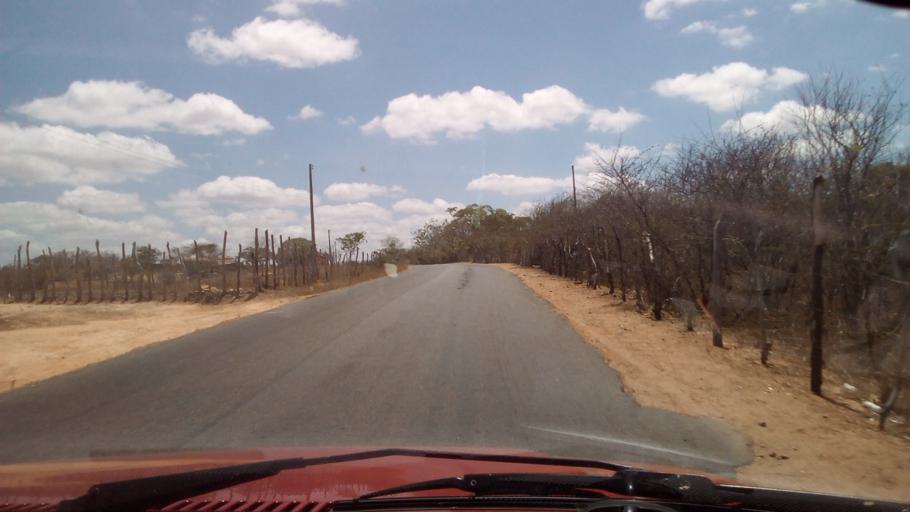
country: BR
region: Paraiba
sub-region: Cacimba De Dentro
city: Cacimba de Dentro
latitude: -6.6159
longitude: -35.8033
